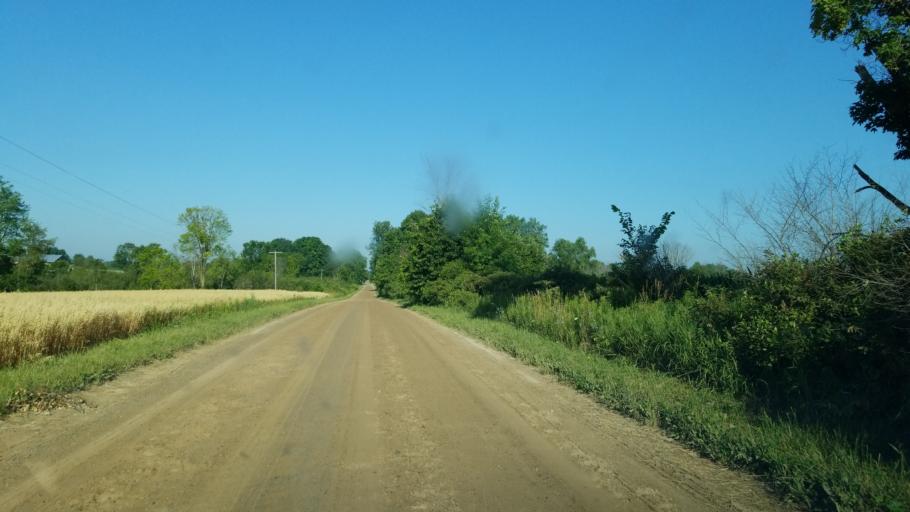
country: US
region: Michigan
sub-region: Mecosta County
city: Canadian Lakes
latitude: 43.5546
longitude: -85.3865
